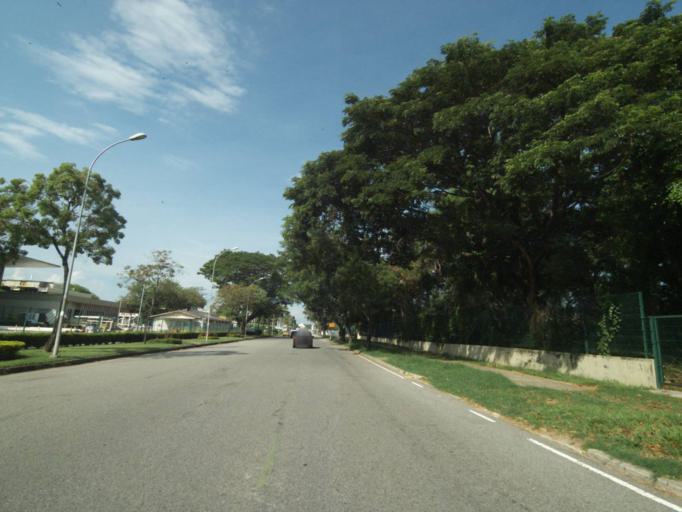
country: BR
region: Rio de Janeiro
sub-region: Rio De Janeiro
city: Rio de Janeiro
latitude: -22.8563
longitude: -43.2339
